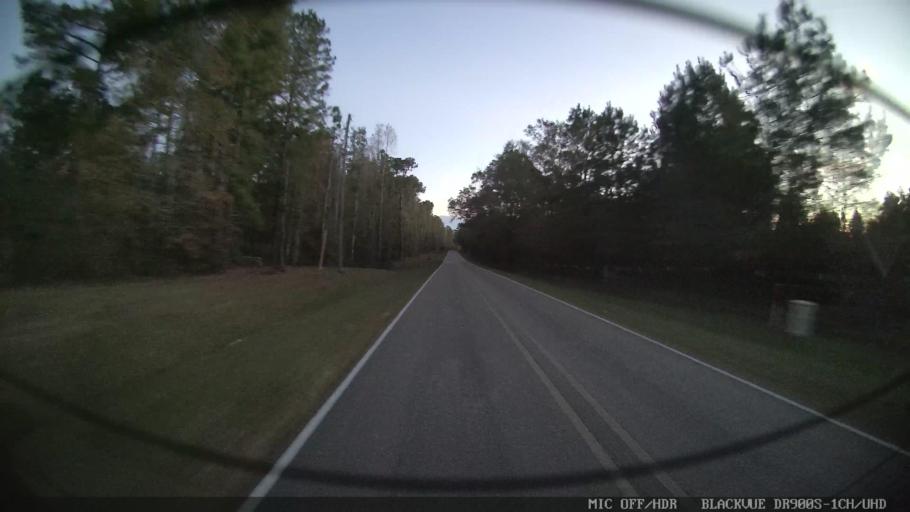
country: US
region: Mississippi
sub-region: Perry County
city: New Augusta
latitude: 31.1322
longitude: -89.1968
